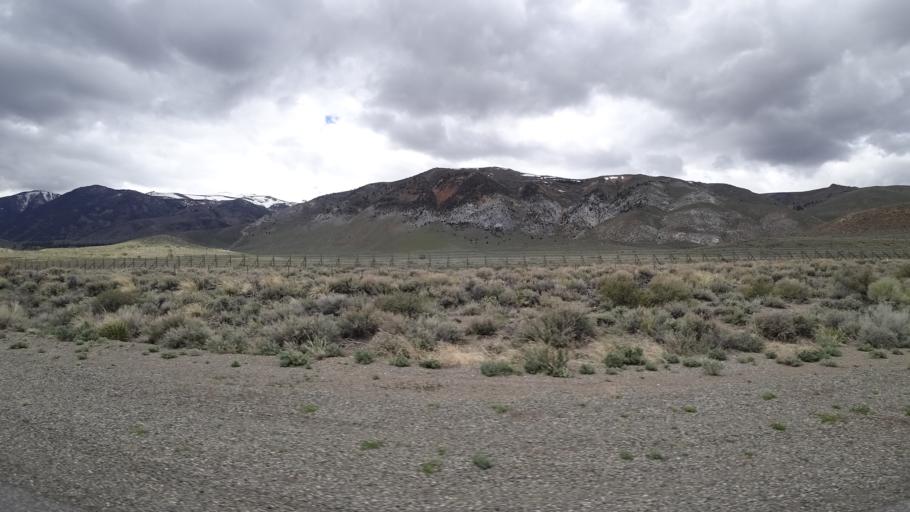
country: US
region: California
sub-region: Mono County
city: Bridgeport
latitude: 38.0517
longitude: -119.1648
